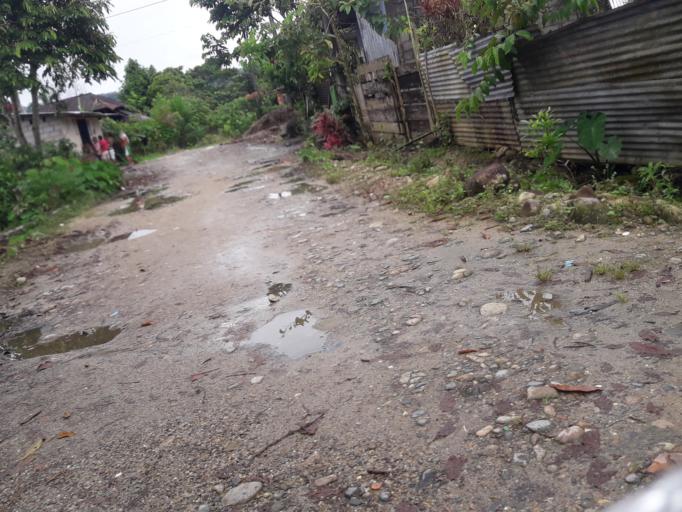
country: EC
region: Napo
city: Tena
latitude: -0.9657
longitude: -77.8537
